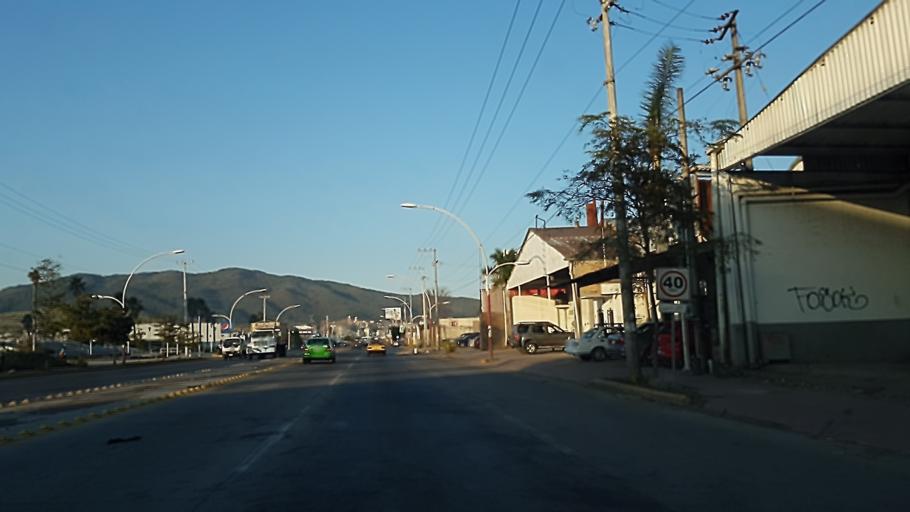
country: MX
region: Nayarit
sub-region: Tepic
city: La Corregidora
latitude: 21.4751
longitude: -104.8477
